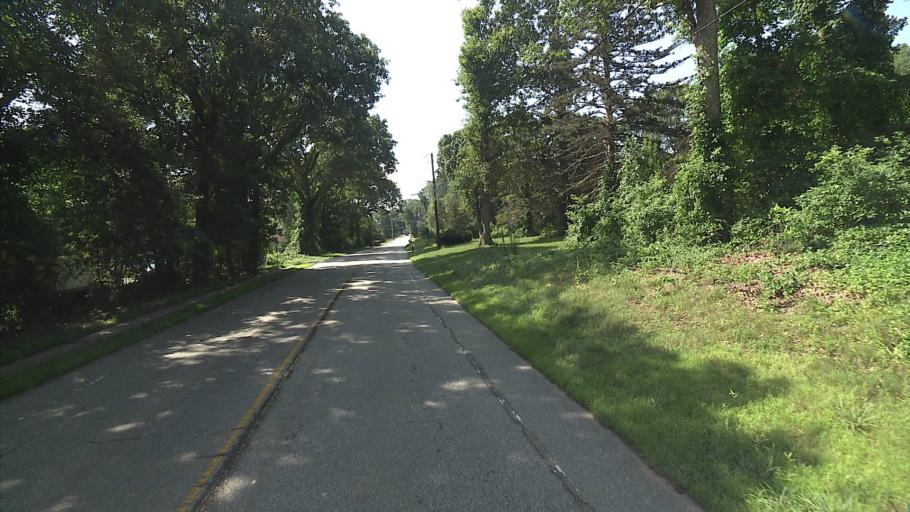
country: US
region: Connecticut
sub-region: Middlesex County
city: Clinton
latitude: 41.2804
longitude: -72.4866
